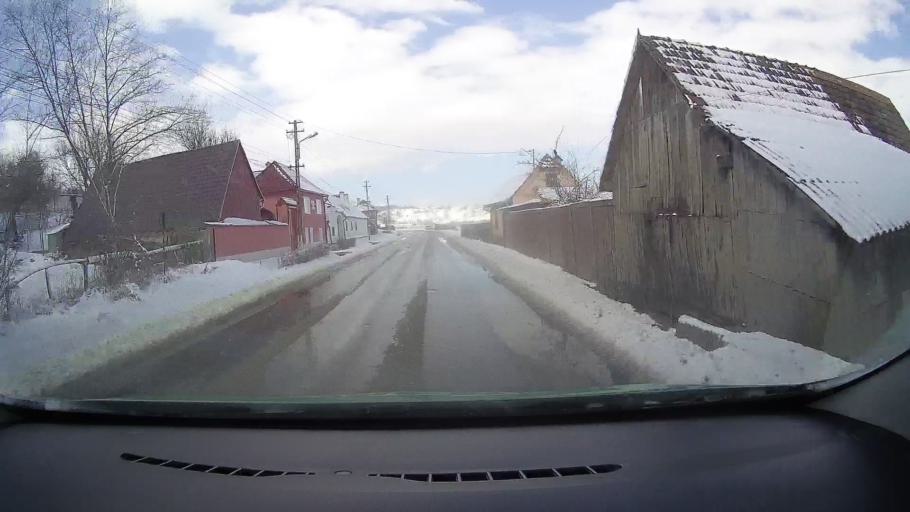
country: RO
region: Sibiu
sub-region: Comuna Altina
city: Altina
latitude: 45.9349
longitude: 24.4629
